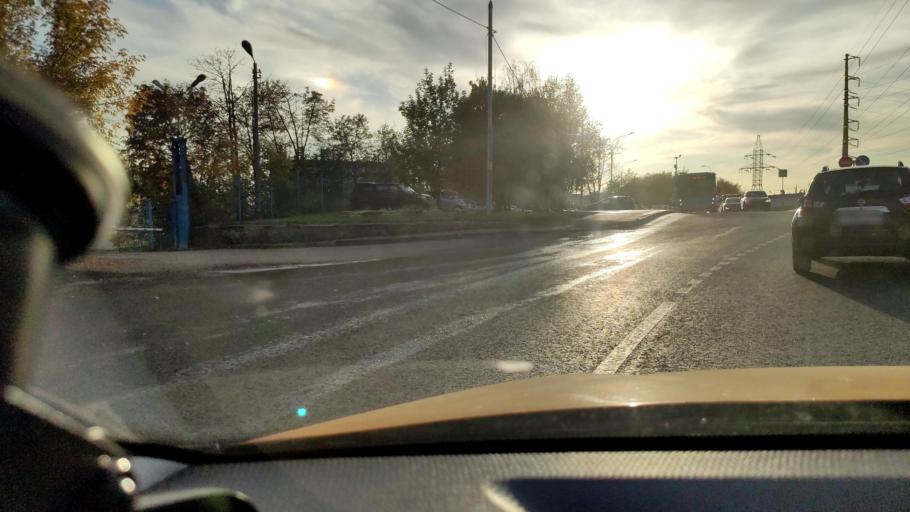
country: RU
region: Moscow
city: Strogino
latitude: 55.8362
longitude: 37.4148
